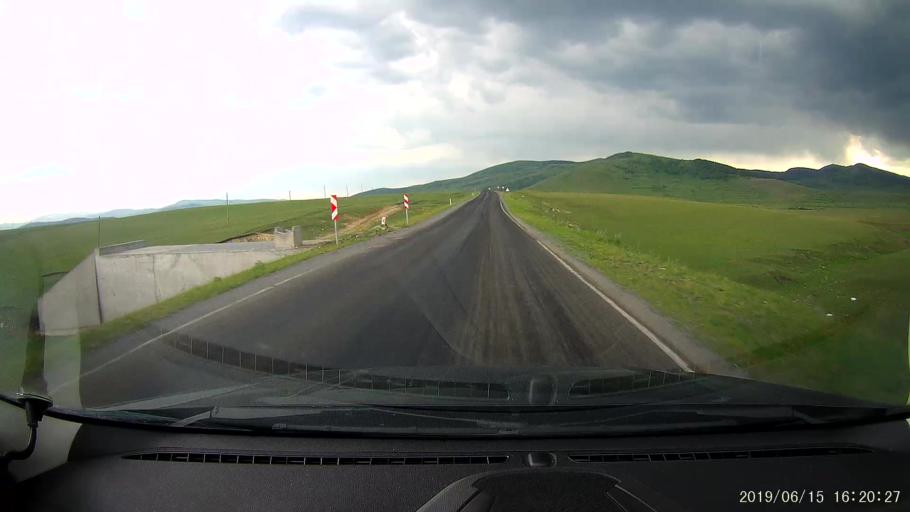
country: TR
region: Ardahan
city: Hanak
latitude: 41.2141
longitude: 42.8480
